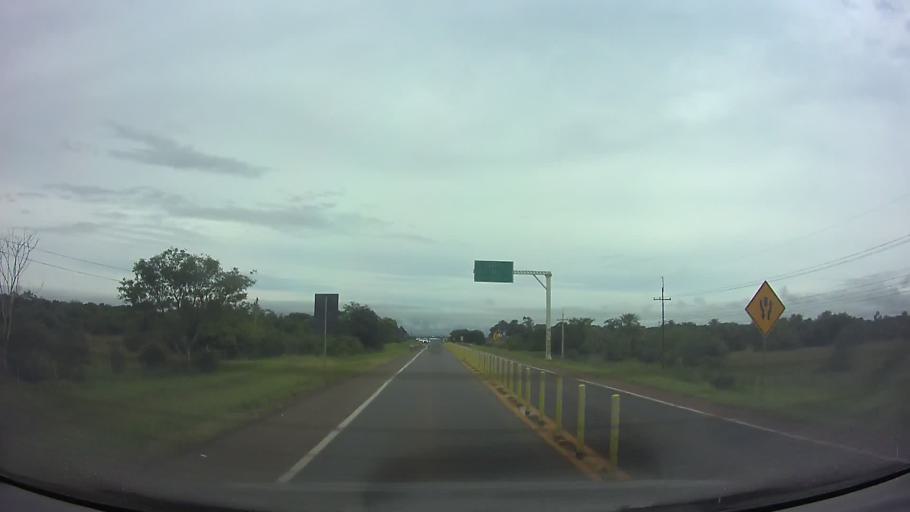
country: PY
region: Paraguari
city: Carapegua
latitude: -25.7506
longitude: -57.2194
